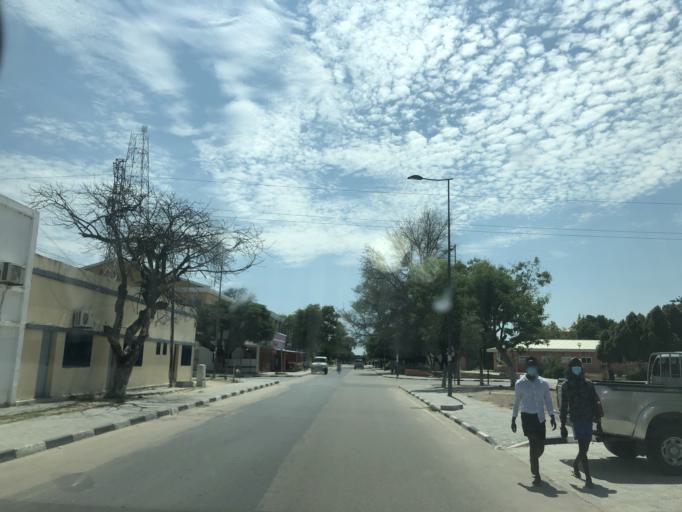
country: AO
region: Cunene
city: Ondjiva
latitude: -17.0668
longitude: 15.7240
